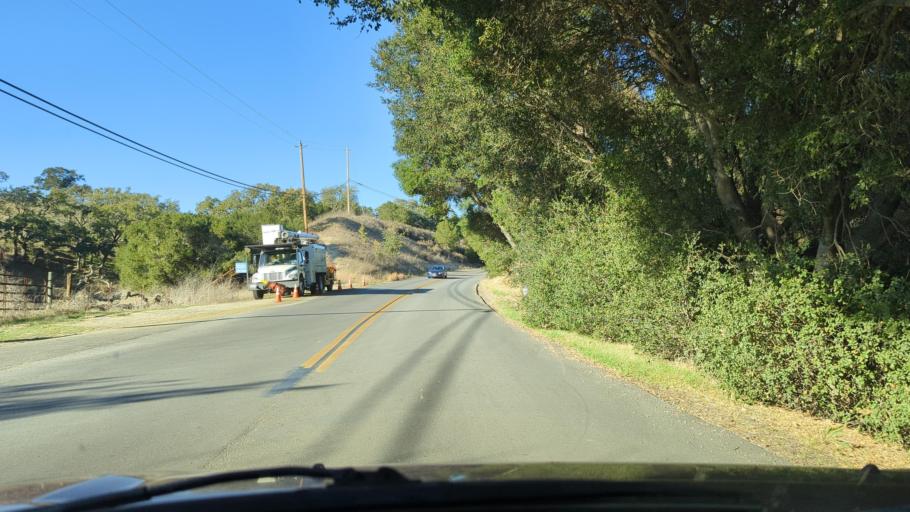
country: US
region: California
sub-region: Santa Barbara County
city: Santa Ynez
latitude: 34.5895
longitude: -120.0996
